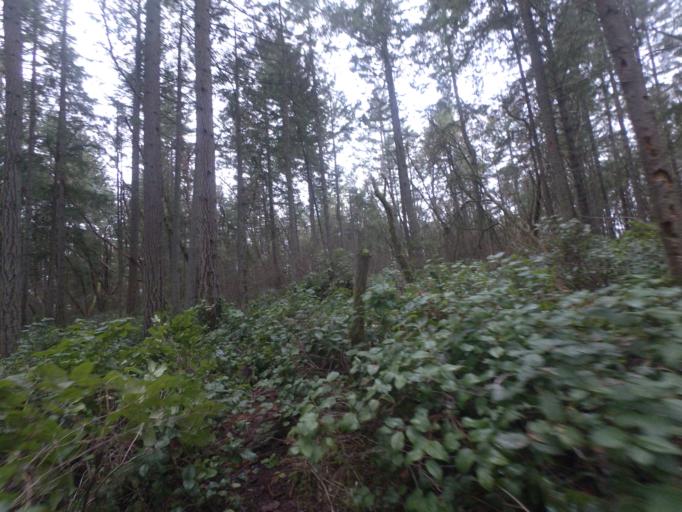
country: US
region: Washington
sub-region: Pierce County
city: University Place
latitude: 47.2066
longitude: -122.5520
